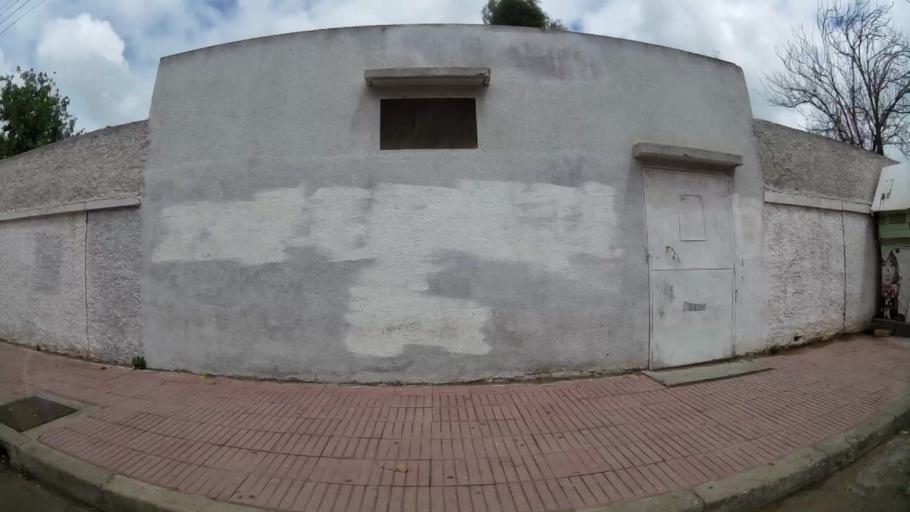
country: MA
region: Grand Casablanca
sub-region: Casablanca
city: Casablanca
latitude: 33.5388
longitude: -7.5963
